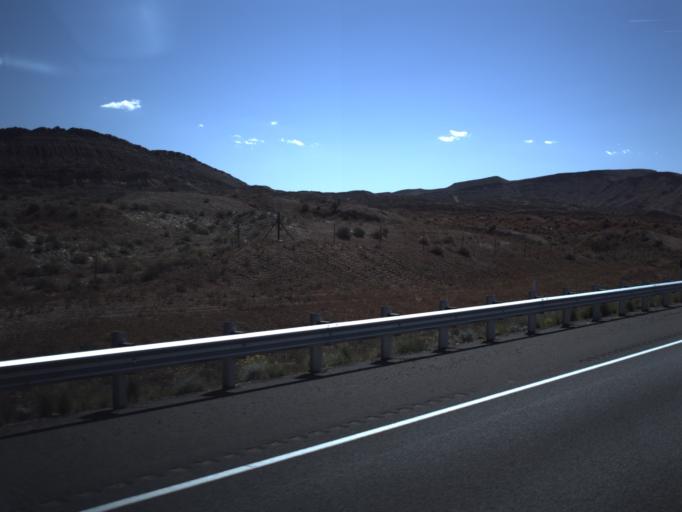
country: US
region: Utah
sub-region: Washington County
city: Washington
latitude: 37.0731
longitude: -113.4858
